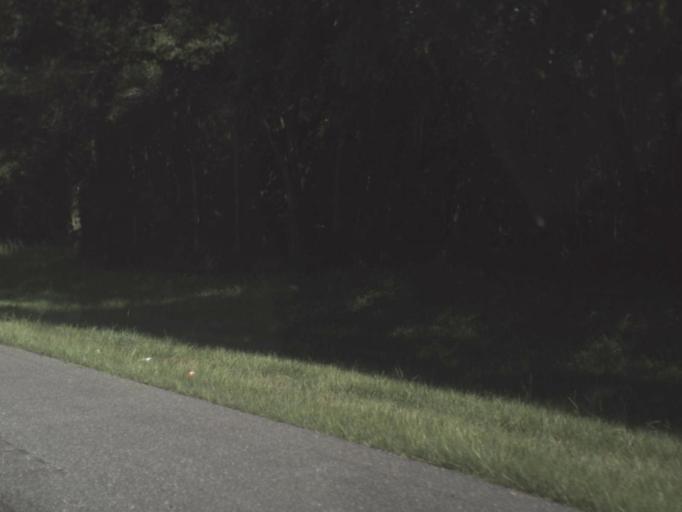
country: US
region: Florida
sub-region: Suwannee County
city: Live Oak
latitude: 30.3382
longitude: -83.1108
